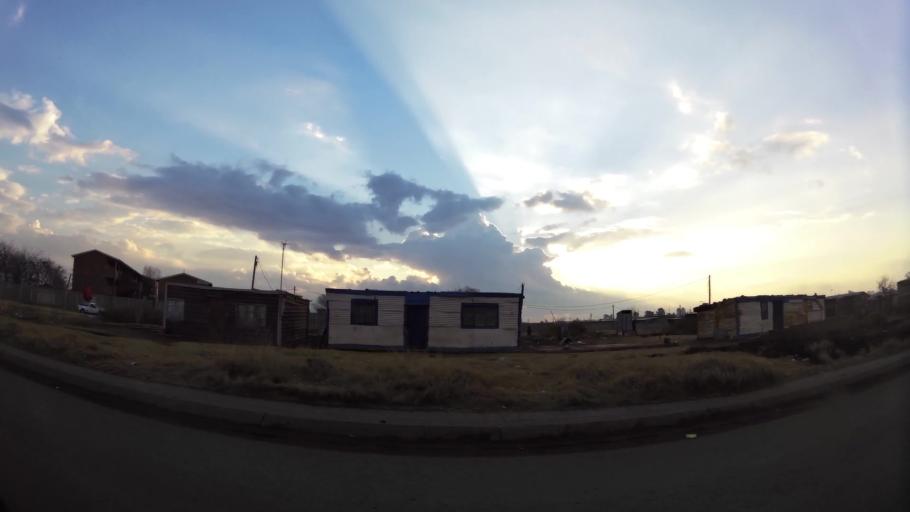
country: ZA
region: Gauteng
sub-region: City of Johannesburg Metropolitan Municipality
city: Orange Farm
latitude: -26.5452
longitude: 27.8427
